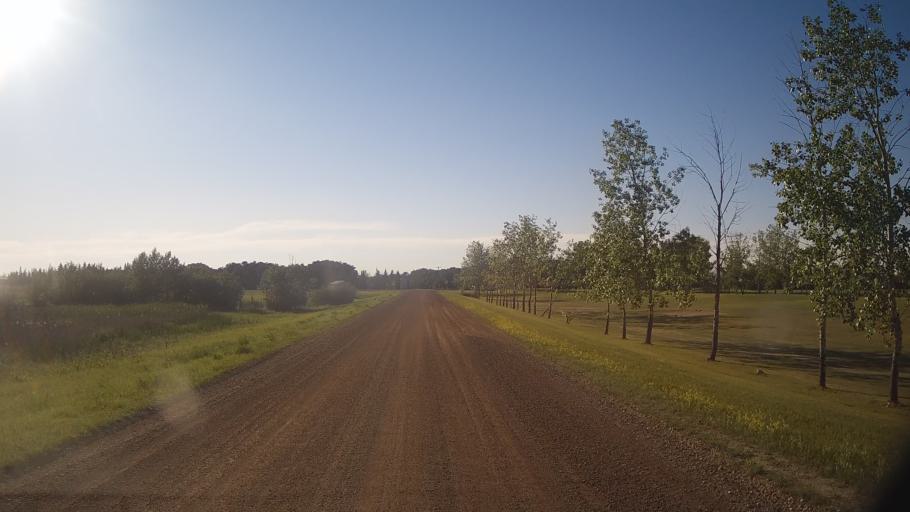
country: CA
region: Saskatchewan
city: Lanigan
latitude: 51.8495
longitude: -105.0149
